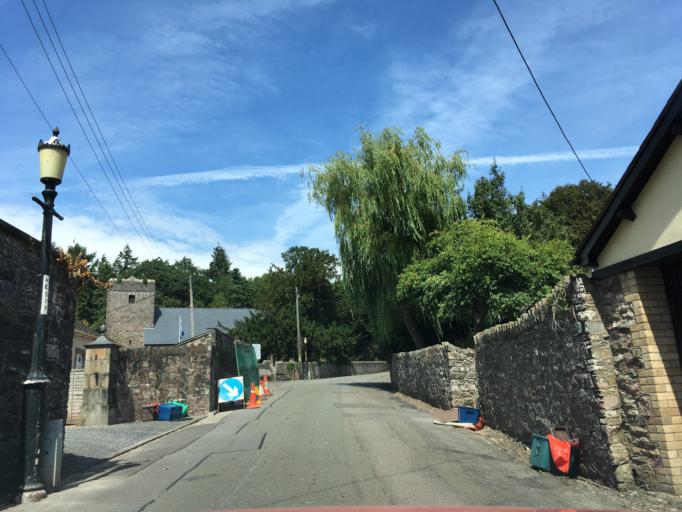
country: GB
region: Wales
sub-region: Caerphilly County Borough
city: Risca
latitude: 51.5855
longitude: -3.1158
